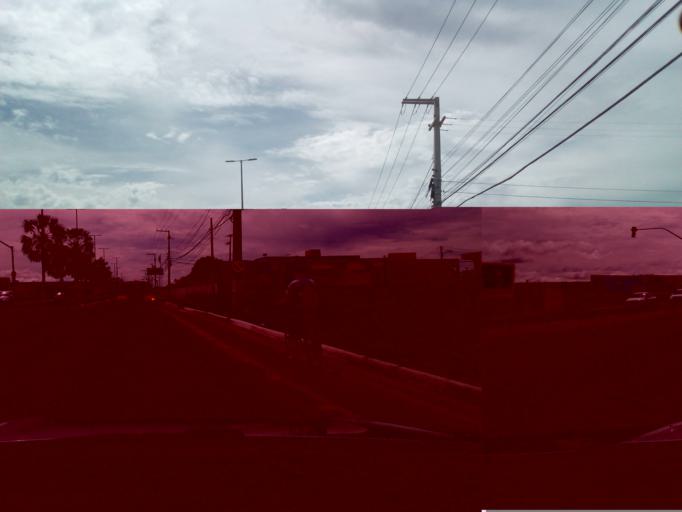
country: BR
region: Rio Grande do Norte
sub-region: Mossoro
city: Mossoro
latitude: -5.1744
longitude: -37.3711
